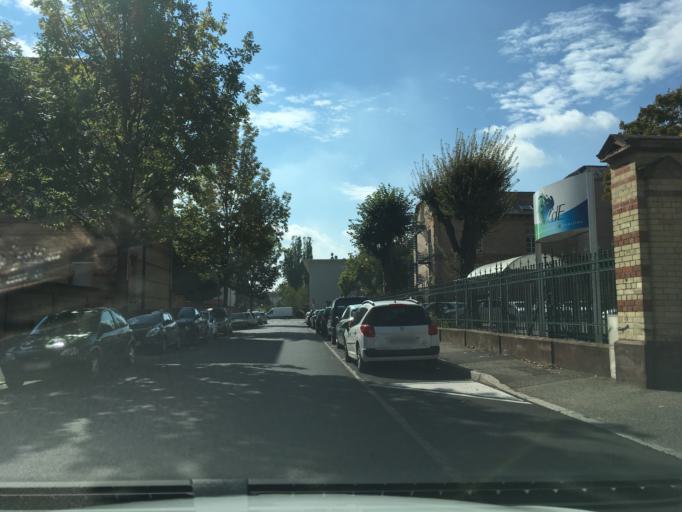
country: FR
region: Alsace
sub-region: Departement du Haut-Rhin
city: Colmar
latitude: 48.0766
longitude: 7.3423
